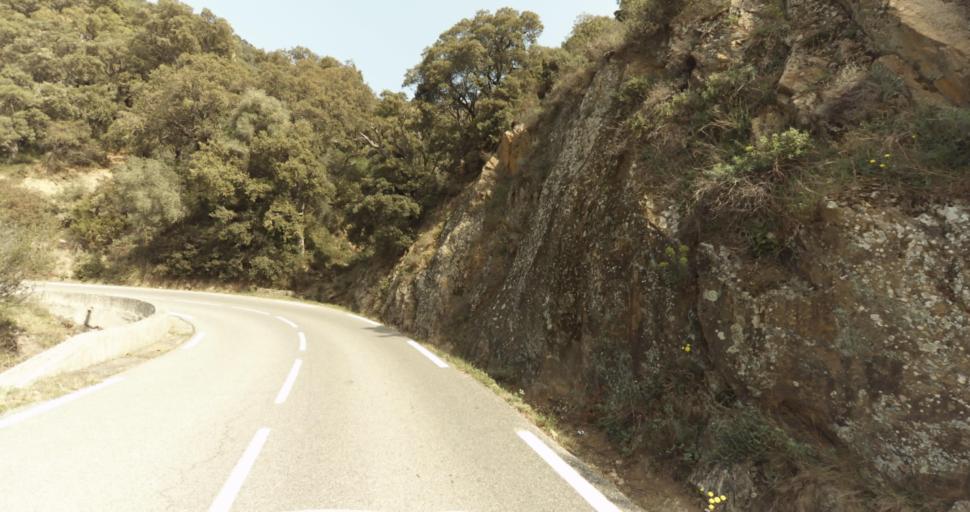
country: FR
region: Provence-Alpes-Cote d'Azur
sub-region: Departement du Var
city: Bormes-les-Mimosas
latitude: 43.1633
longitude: 6.3442
